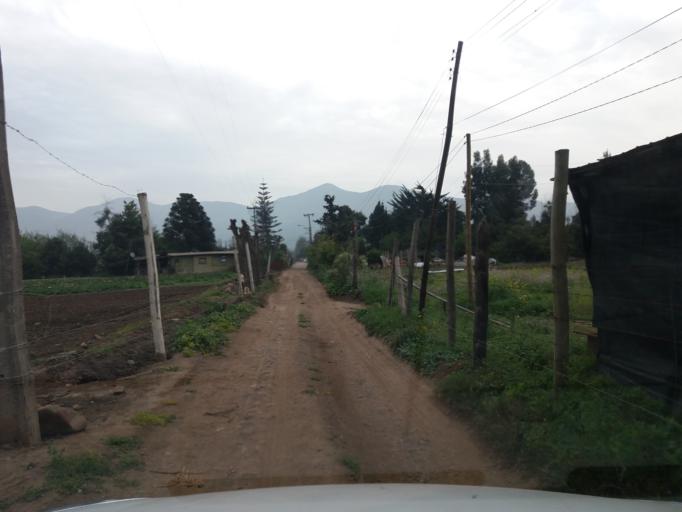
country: CL
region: Valparaiso
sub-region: Provincia de Quillota
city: Hacienda La Calera
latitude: -32.8188
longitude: -71.1305
